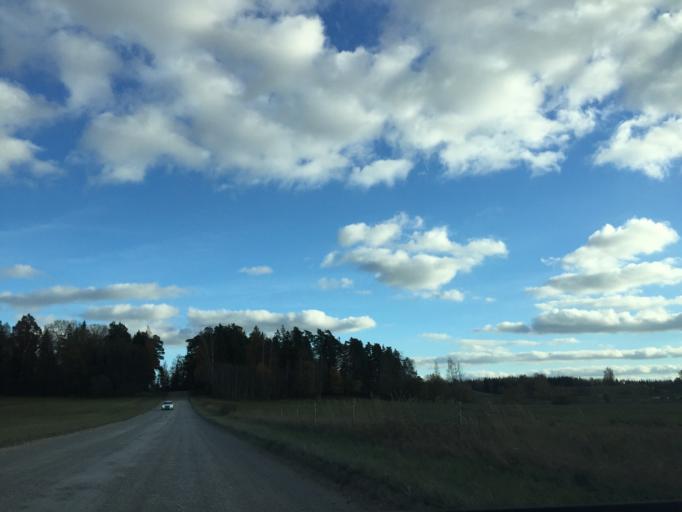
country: LV
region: Tukuma Rajons
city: Tukums
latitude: 56.9648
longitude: 22.9699
